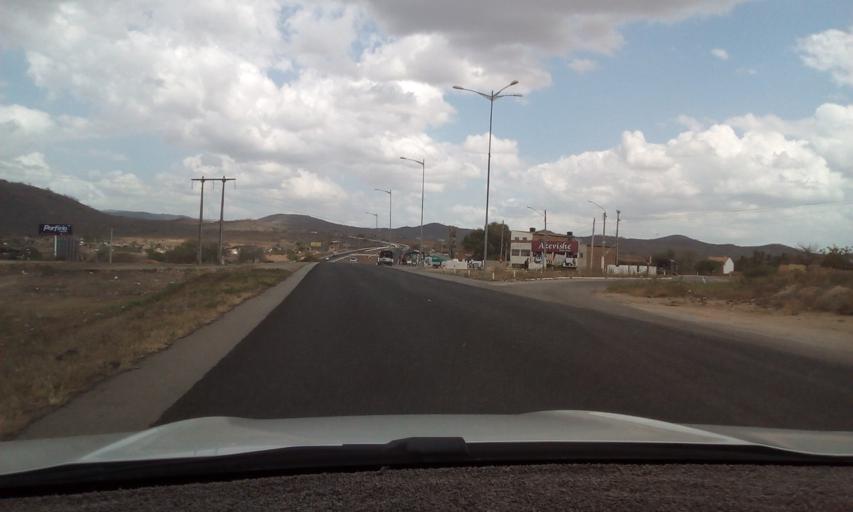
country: BR
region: Pernambuco
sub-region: Toritama
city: Toritama
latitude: -8.1067
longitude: -36.0223
